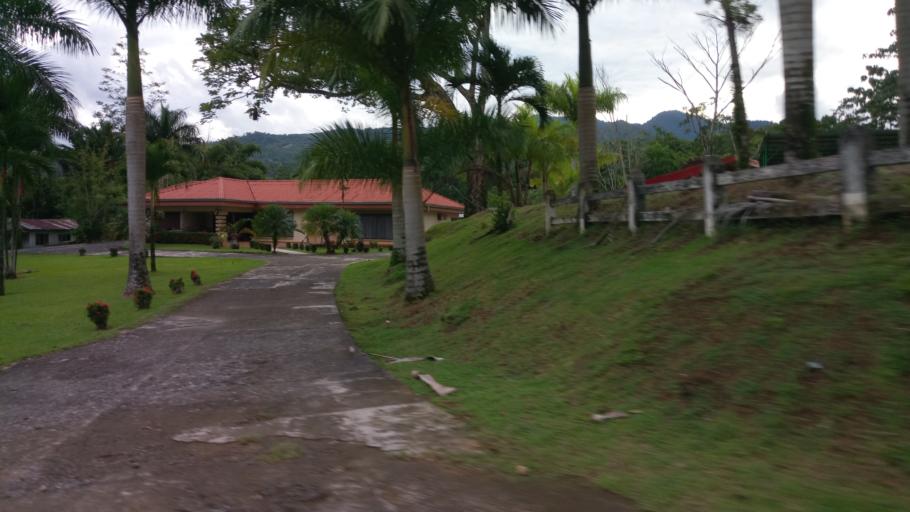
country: CR
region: Alajuela
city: Pocosol
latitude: 10.3600
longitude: -84.5898
